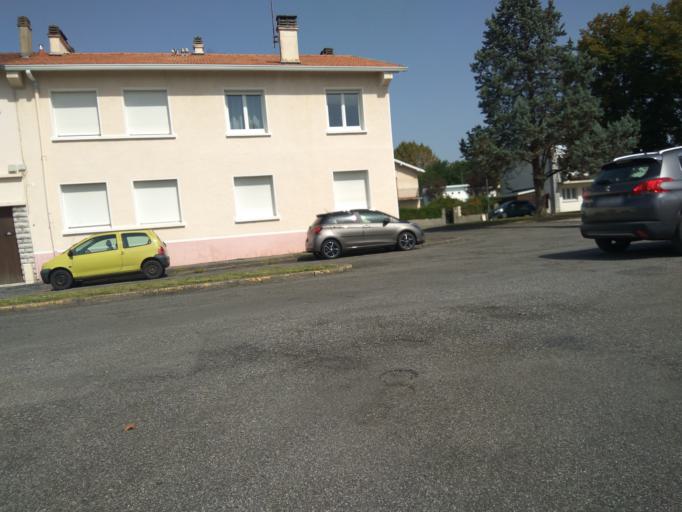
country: FR
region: Aquitaine
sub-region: Departement des Pyrenees-Atlantiques
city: Bizanos
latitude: 43.2918
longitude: -0.3501
